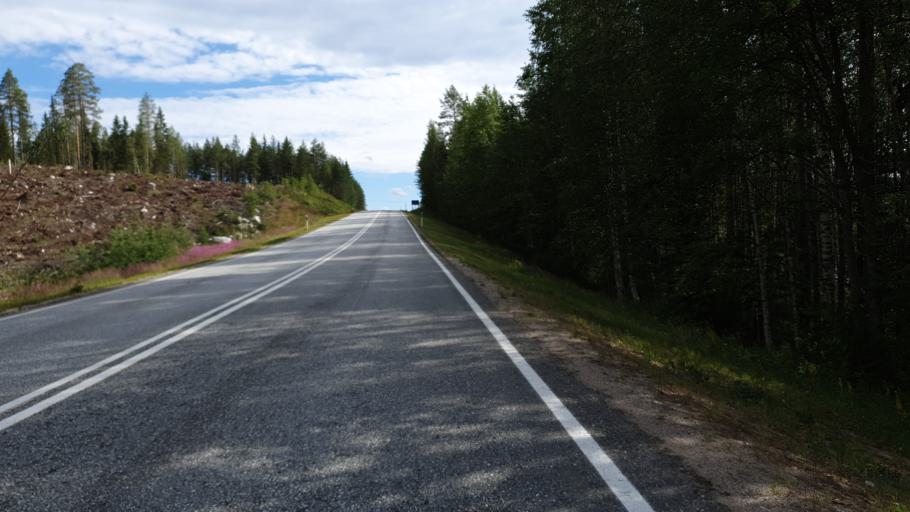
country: FI
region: Kainuu
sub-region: Kehys-Kainuu
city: Kuhmo
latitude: 64.4943
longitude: 29.9026
